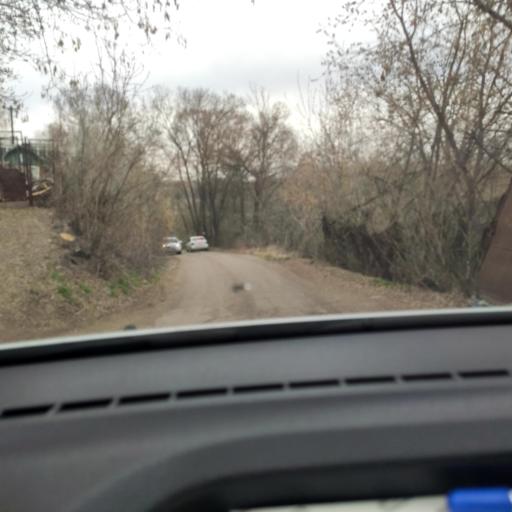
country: RU
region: Bashkortostan
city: Avdon
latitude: 54.6233
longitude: 55.5985
